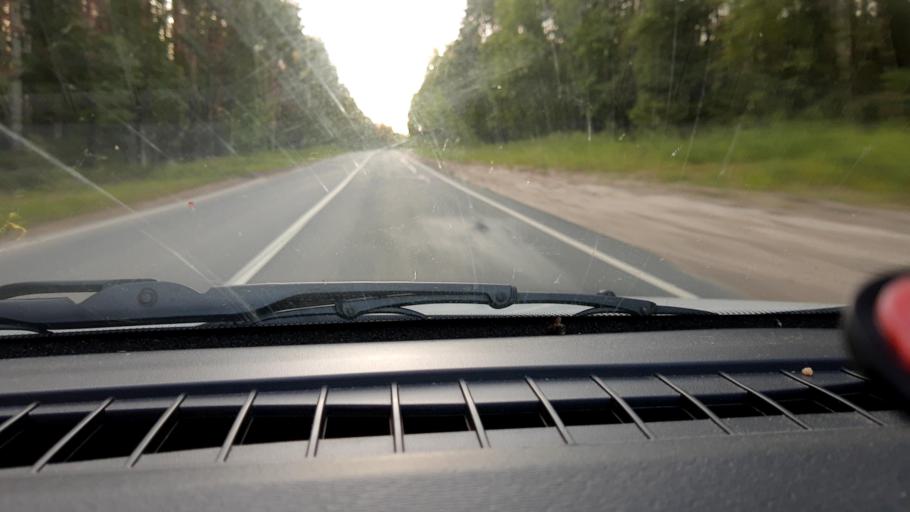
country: RU
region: Nizjnij Novgorod
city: Krasnyye Baki
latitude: 56.9892
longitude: 45.1168
